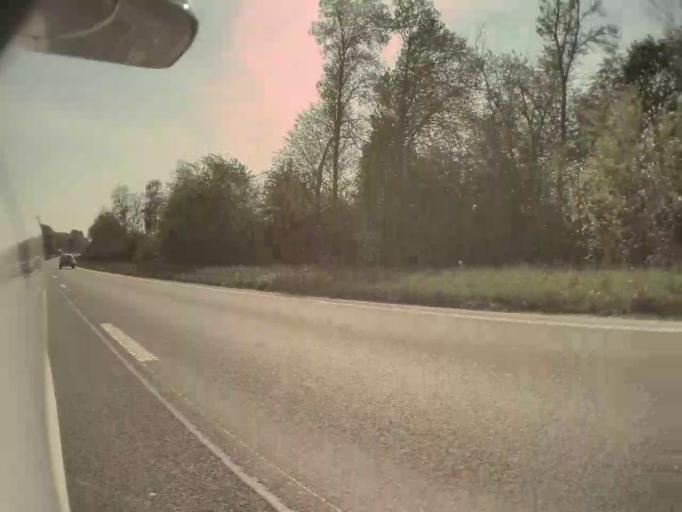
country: BE
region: Wallonia
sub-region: Province de Namur
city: Ciney
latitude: 50.2977
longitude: 5.1183
